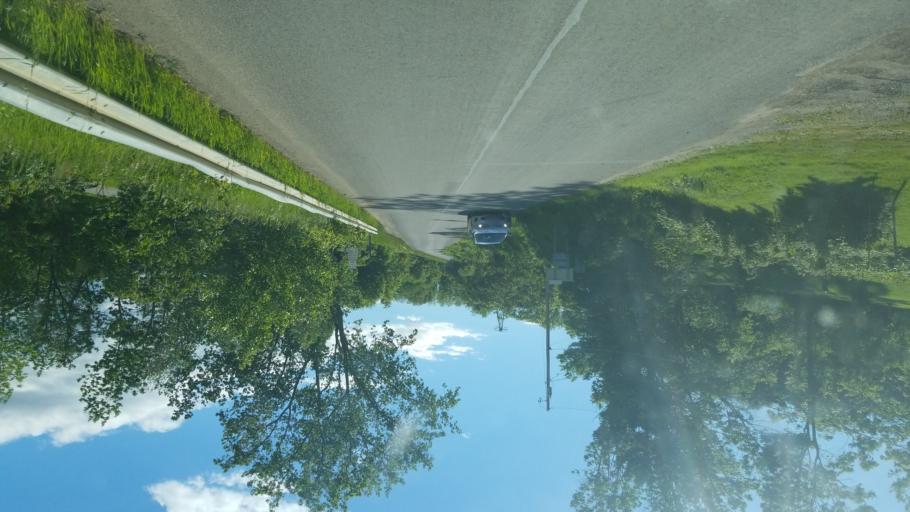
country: US
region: New York
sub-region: Montgomery County
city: Saint Johnsville
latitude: 42.9964
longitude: -74.7398
